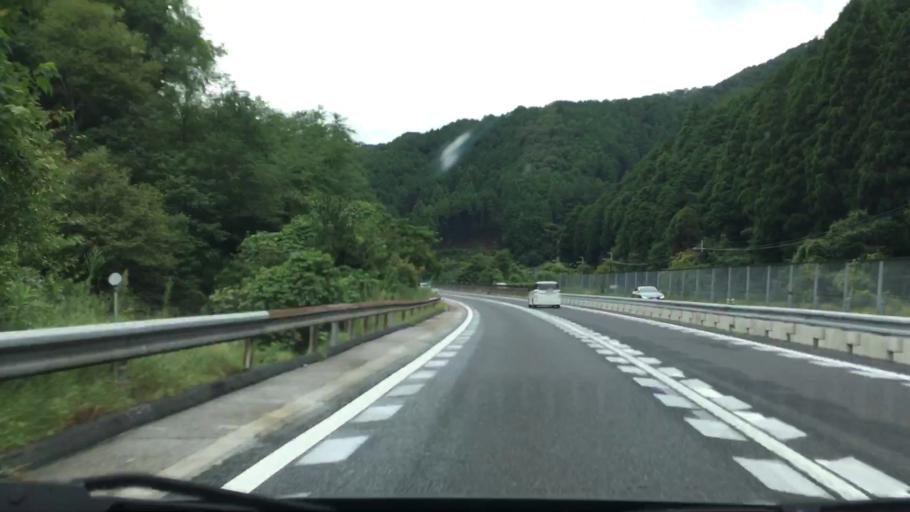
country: JP
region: Hyogo
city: Yamazakicho-nakabirose
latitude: 35.0465
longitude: 134.4610
